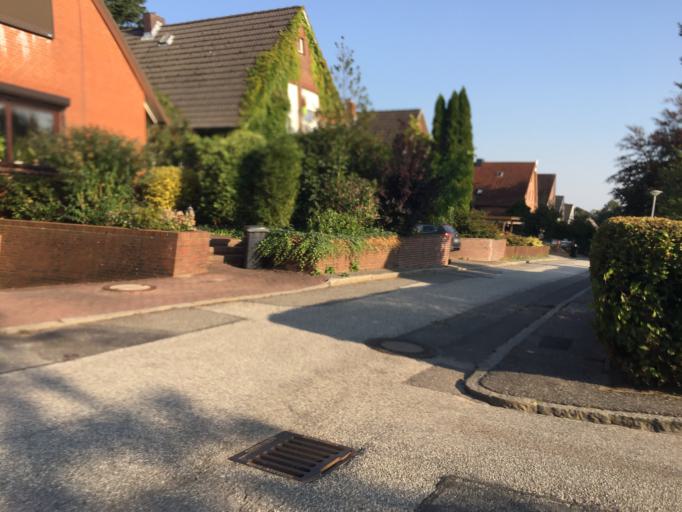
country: DE
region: Schleswig-Holstein
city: Oelixdorf
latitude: 53.9293
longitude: 9.5414
